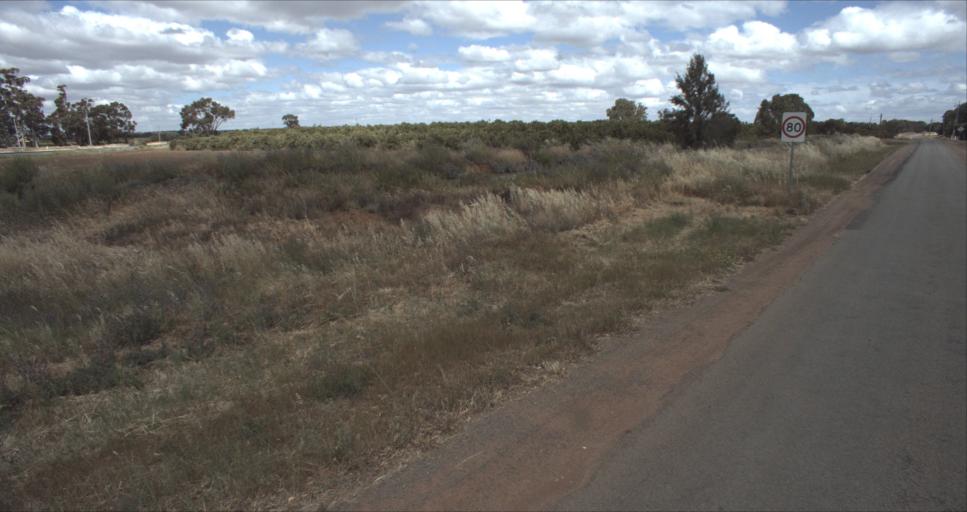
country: AU
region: New South Wales
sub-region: Leeton
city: Leeton
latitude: -34.5793
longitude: 146.3972
